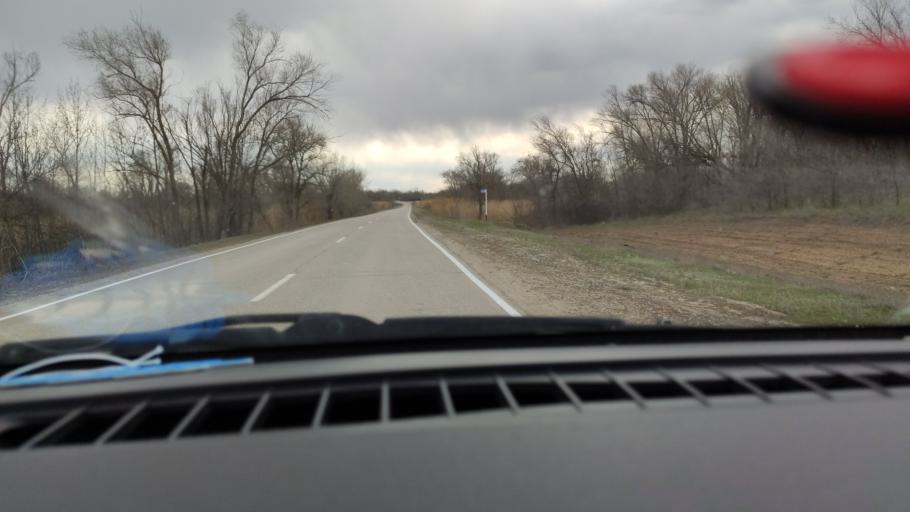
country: RU
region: Saratov
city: Privolzhskiy
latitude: 51.2364
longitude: 45.9233
